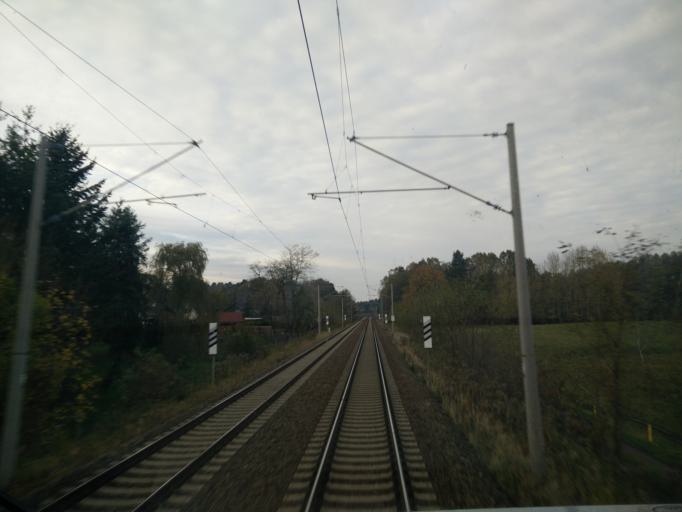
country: DE
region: Brandenburg
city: Halbe
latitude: 52.0915
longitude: 13.7188
